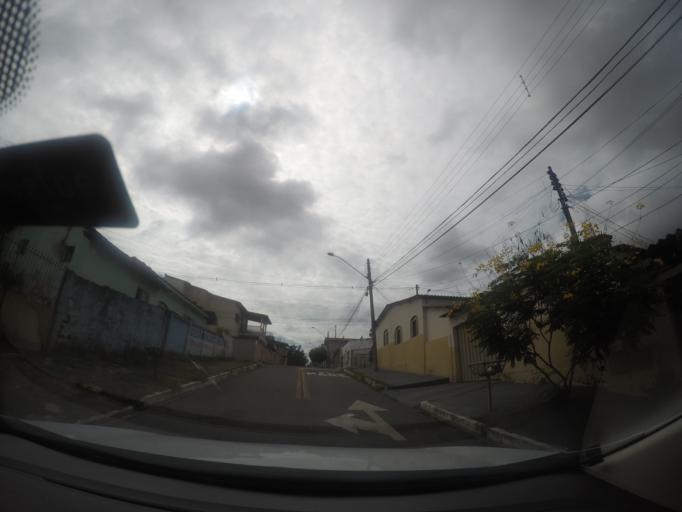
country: BR
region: Goias
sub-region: Goiania
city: Goiania
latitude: -16.6663
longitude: -49.2960
